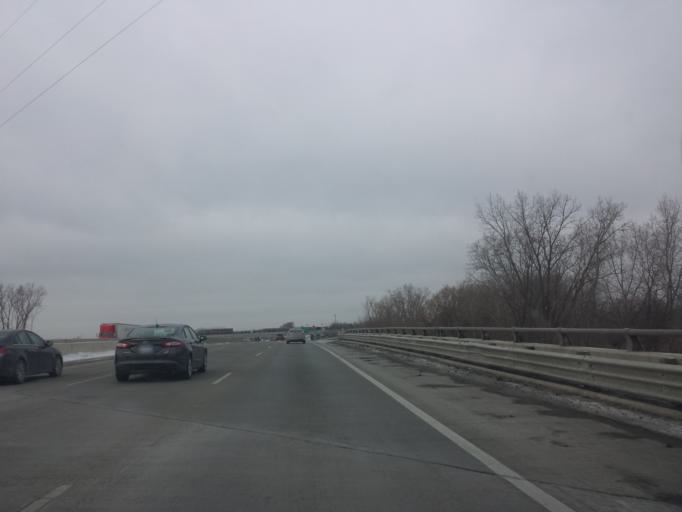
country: US
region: Michigan
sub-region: Oakland County
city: Rochester Hills
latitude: 42.6442
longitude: -83.1885
